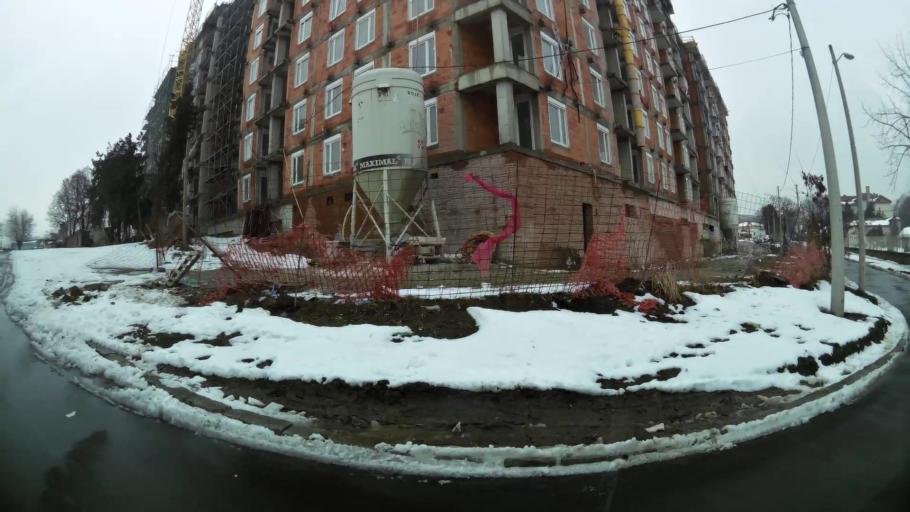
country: RS
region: Central Serbia
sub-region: Belgrade
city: Zemun
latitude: 44.8543
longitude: 20.3820
